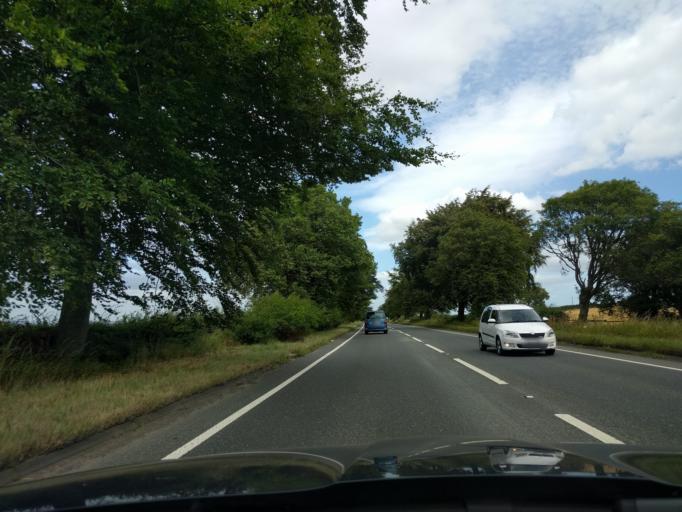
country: GB
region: England
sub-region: Northumberland
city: Hebron
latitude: 55.2037
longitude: -1.7116
